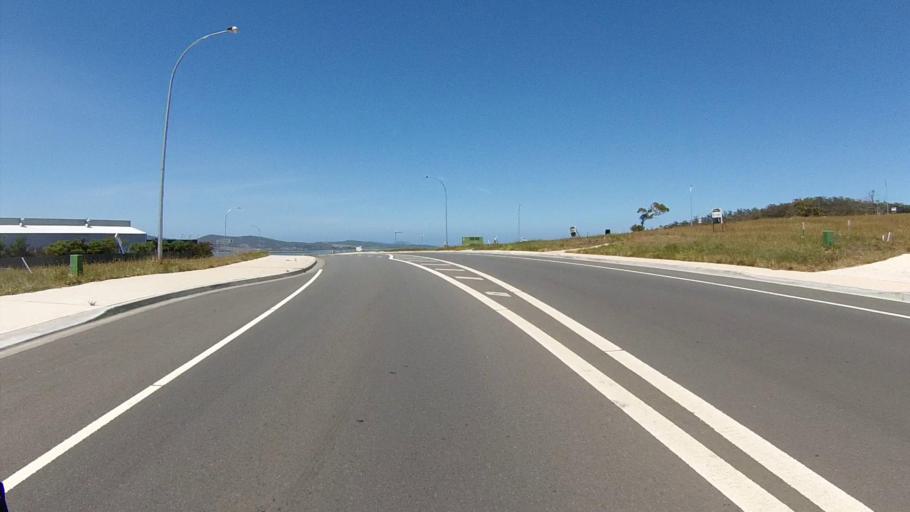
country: AU
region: Tasmania
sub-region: Clarence
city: Rokeby
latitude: -42.8895
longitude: 147.4290
